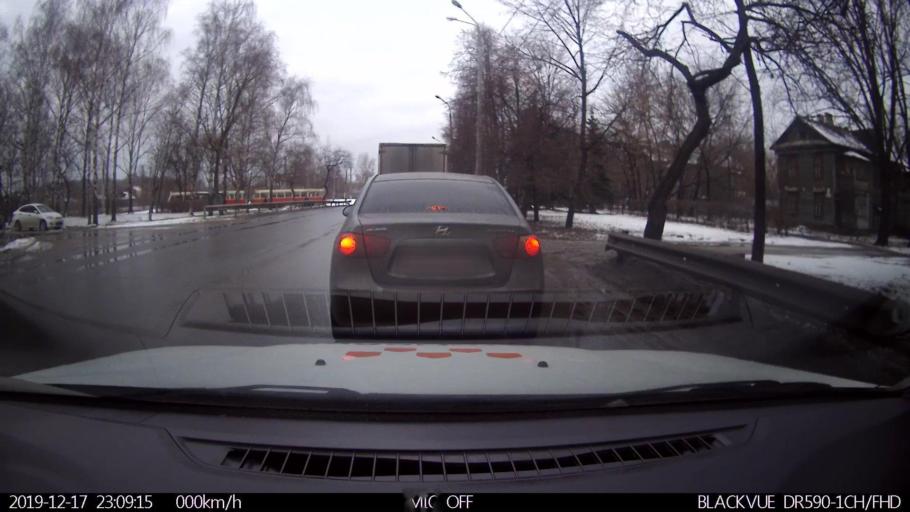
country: RU
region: Nizjnij Novgorod
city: Gorbatovka
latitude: 56.3464
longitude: 43.8389
